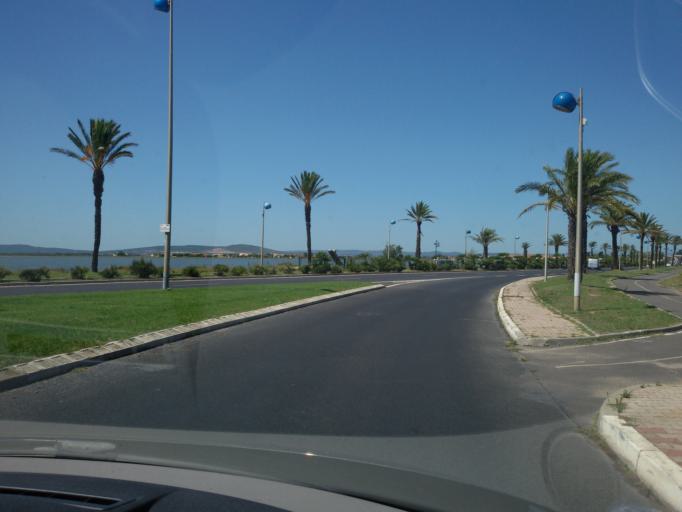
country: FR
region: Languedoc-Roussillon
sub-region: Departement de l'Herault
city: Palavas-les-Flots
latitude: 43.5304
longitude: 3.9229
